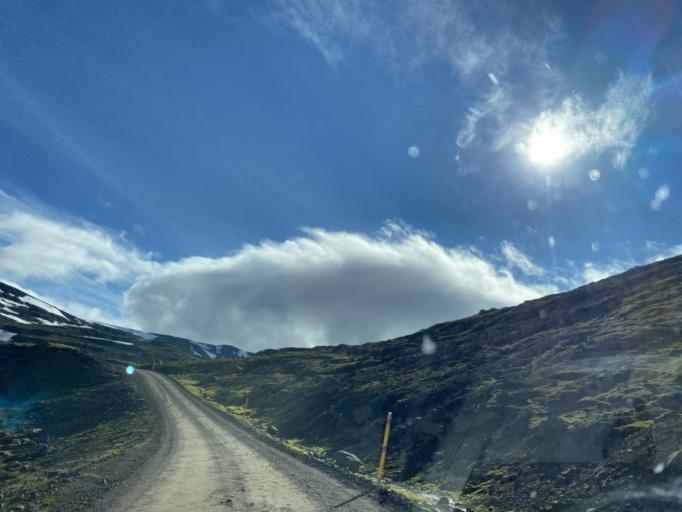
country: IS
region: East
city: Eskifjoerdur
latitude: 65.1726
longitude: -14.1188
